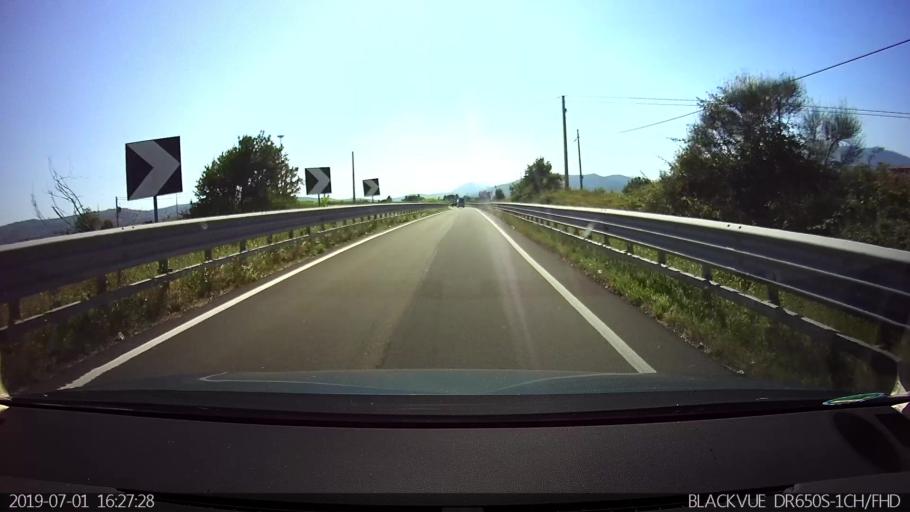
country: IT
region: Latium
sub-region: Provincia di Latina
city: Roccasecca dei Volsci
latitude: 41.4966
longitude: 13.2121
